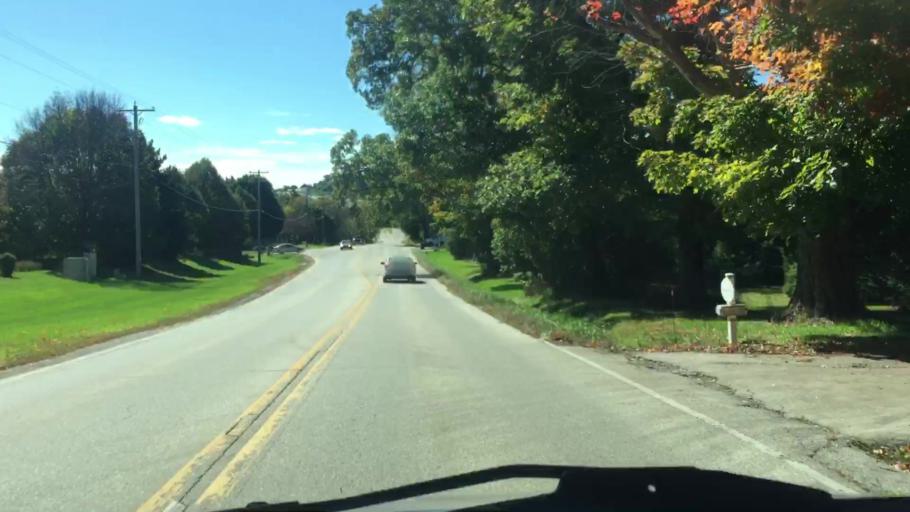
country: US
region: Wisconsin
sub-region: Waukesha County
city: Pewaukee
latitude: 43.0575
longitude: -88.2837
